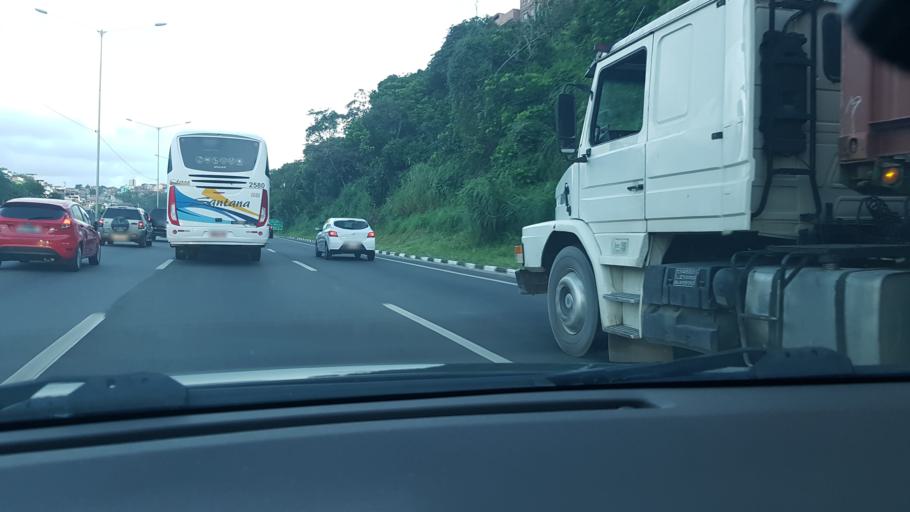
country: BR
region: Bahia
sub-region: Salvador
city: Salvador
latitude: -12.9376
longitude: -38.4723
